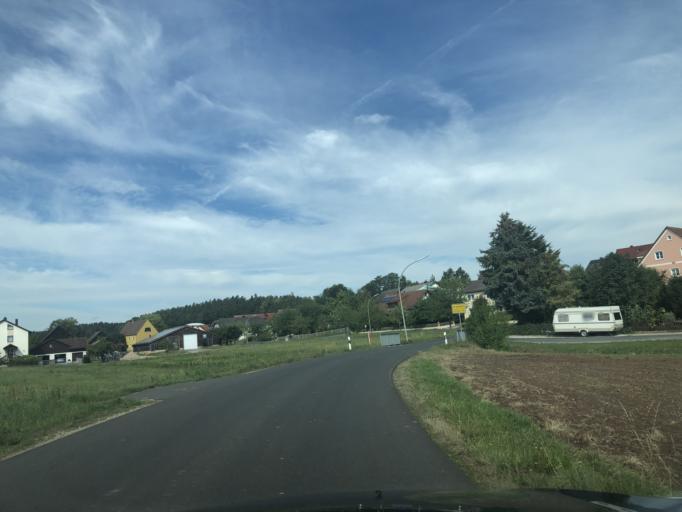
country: DE
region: Bavaria
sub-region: Upper Palatinate
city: Trabitz
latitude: 49.8004
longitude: 11.8728
